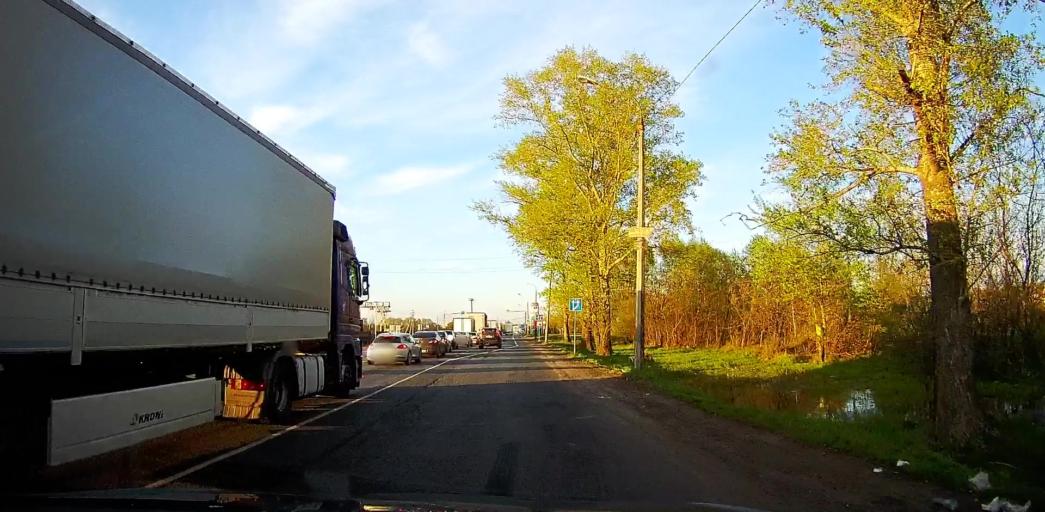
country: RU
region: Moskovskaya
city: Troitskoye
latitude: 55.2766
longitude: 38.4900
